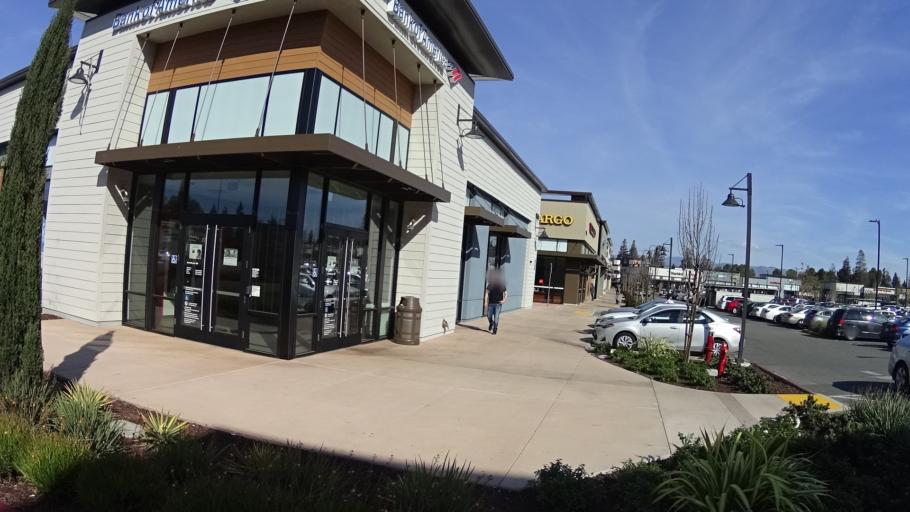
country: US
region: California
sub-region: Santa Clara County
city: San Jose
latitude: 37.3824
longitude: -121.8980
